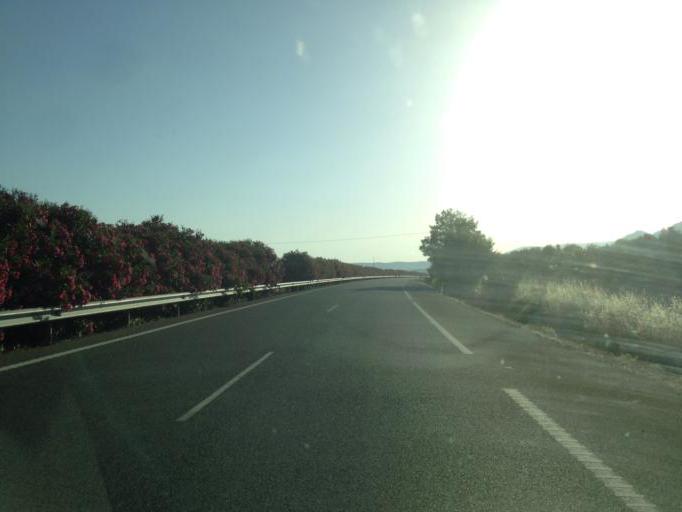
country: ES
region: Andalusia
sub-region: Provincia de Malaga
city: Villanueva del Trabuco
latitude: 37.0478
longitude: -4.3745
